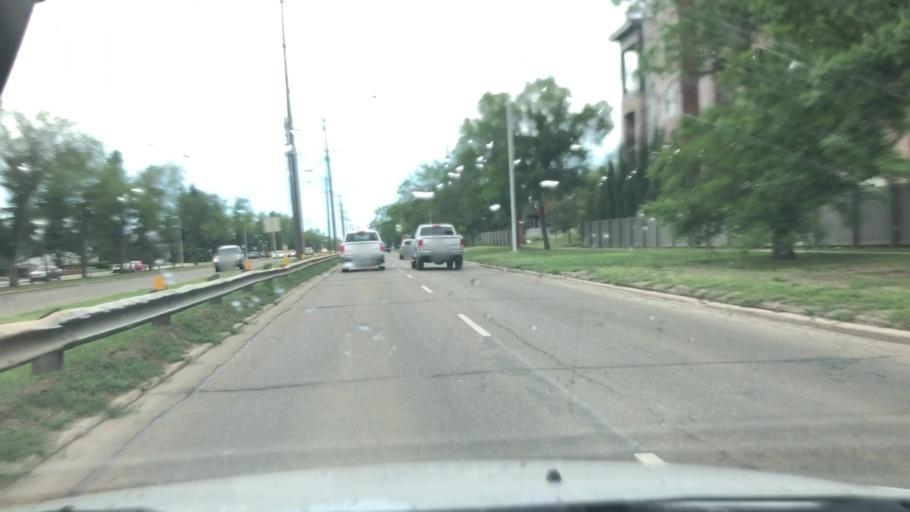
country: CA
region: Alberta
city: Edmonton
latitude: 53.5995
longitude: -113.4981
